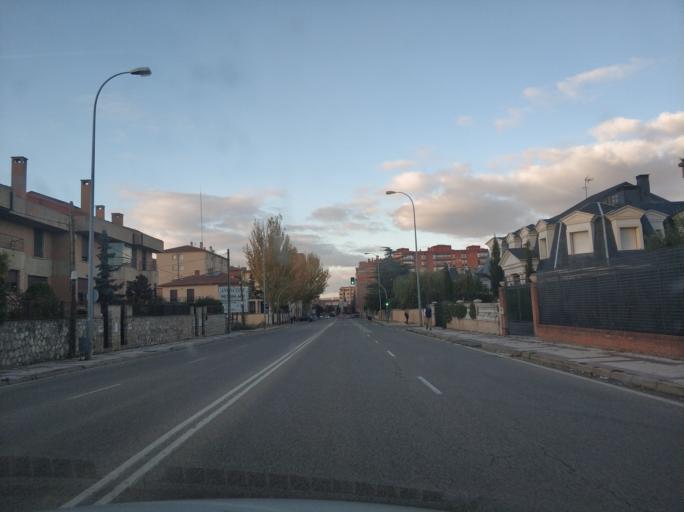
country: ES
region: Castille and Leon
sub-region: Provincia de Soria
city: Soria
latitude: 41.7638
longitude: -2.4787
